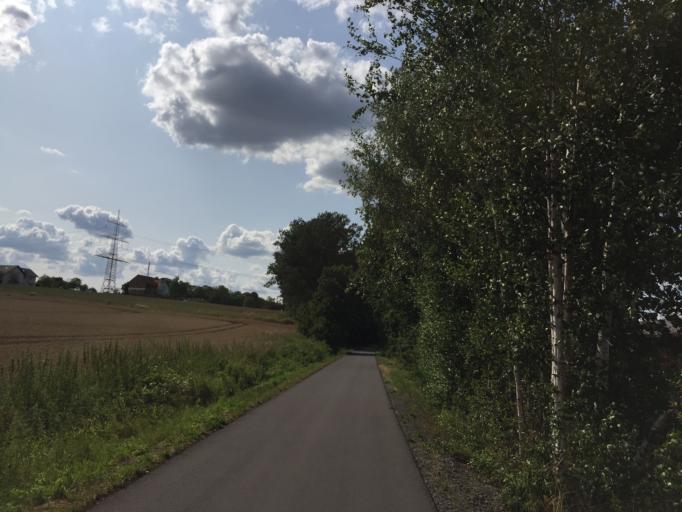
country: DE
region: Hesse
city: Schwalmstadt
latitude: 50.9076
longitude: 9.2118
